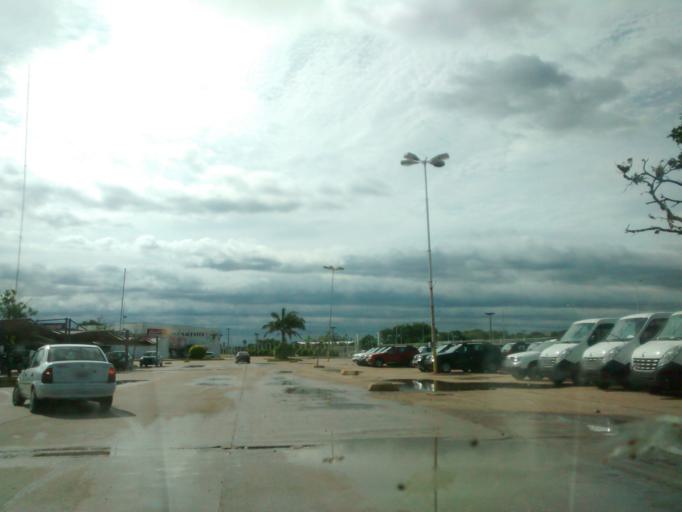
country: AR
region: Chaco
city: Resistencia
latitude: -27.4135
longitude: -58.9690
